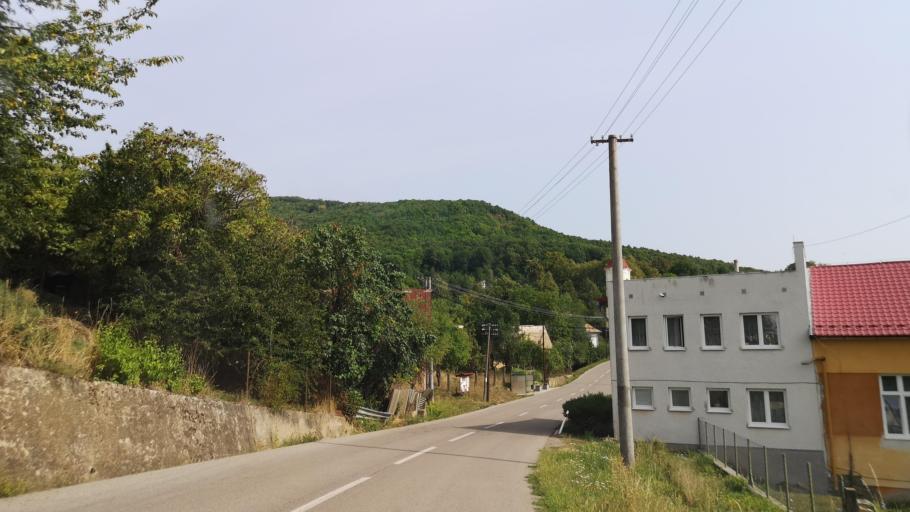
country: SK
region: Banskobystricky
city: Revuca
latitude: 48.6006
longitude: 20.1480
